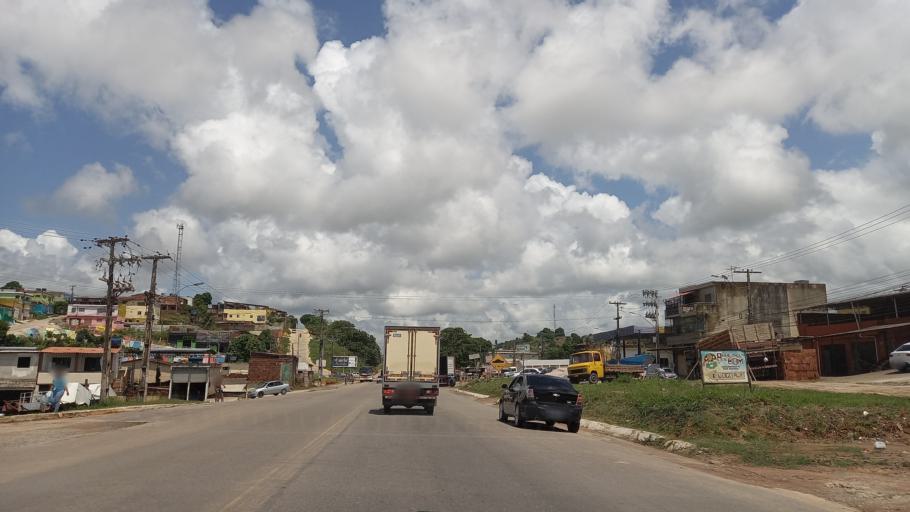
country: BR
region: Pernambuco
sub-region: Jaboatao Dos Guararapes
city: Jaboatao
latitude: -8.2400
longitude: -34.9860
